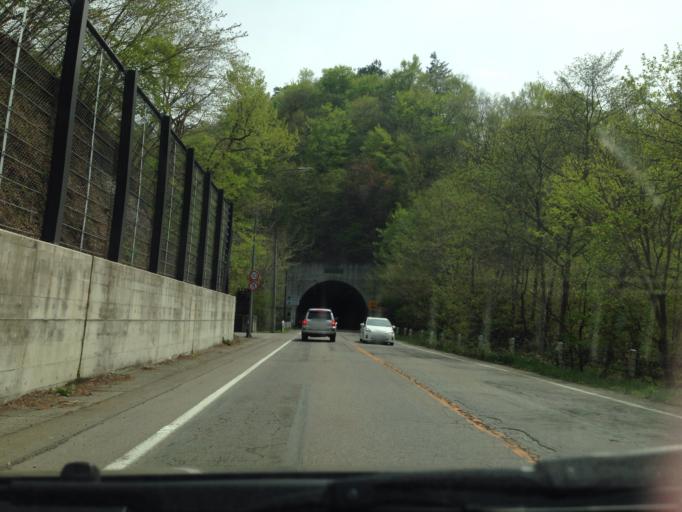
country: JP
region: Tochigi
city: Kuroiso
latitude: 37.0743
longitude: 139.7482
